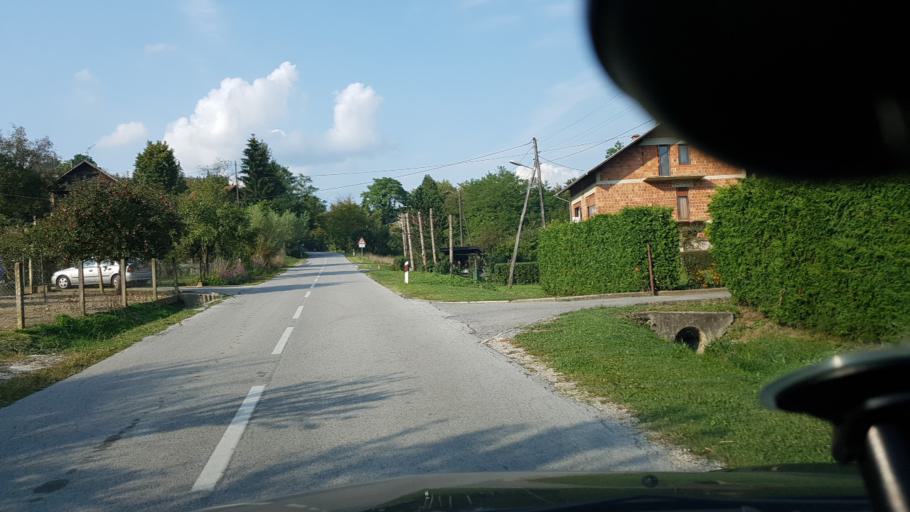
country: SI
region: Bistrica ob Sotli
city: Bistrica ob Sotli
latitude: 46.0581
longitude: 15.7715
